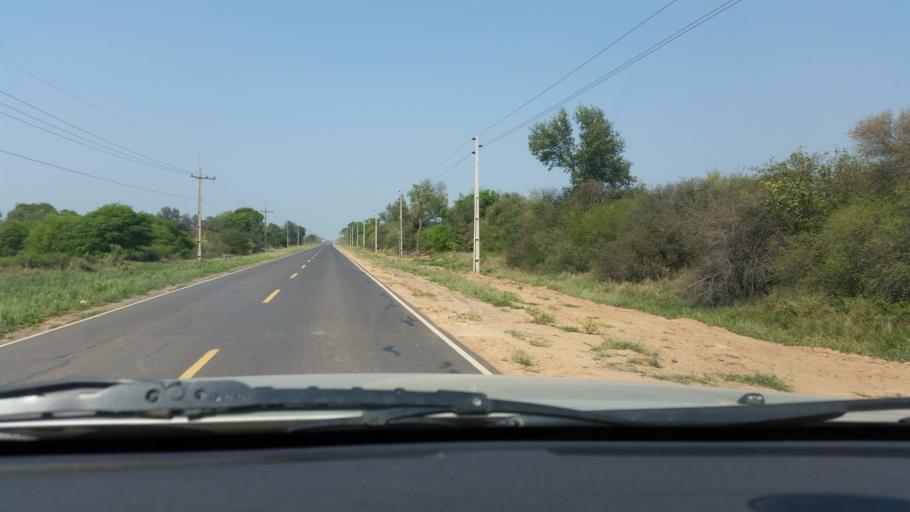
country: PY
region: Boqueron
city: Colonia Neuland
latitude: -22.6118
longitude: -60.1078
